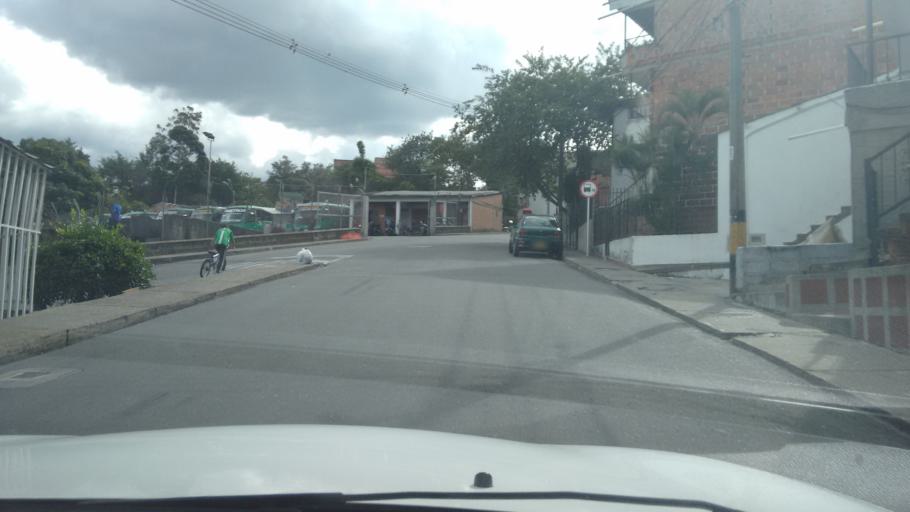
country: CO
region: Antioquia
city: Bello
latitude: 6.2977
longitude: -75.5782
